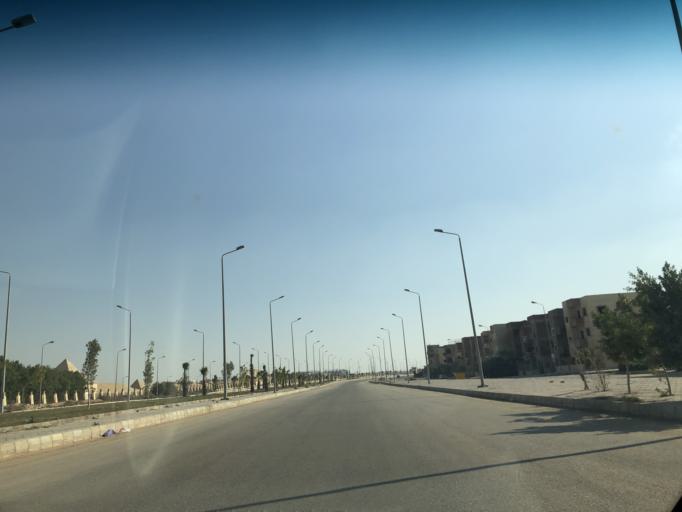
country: EG
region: Al Jizah
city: Madinat Sittah Uktubar
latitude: 29.9328
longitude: 31.0669
